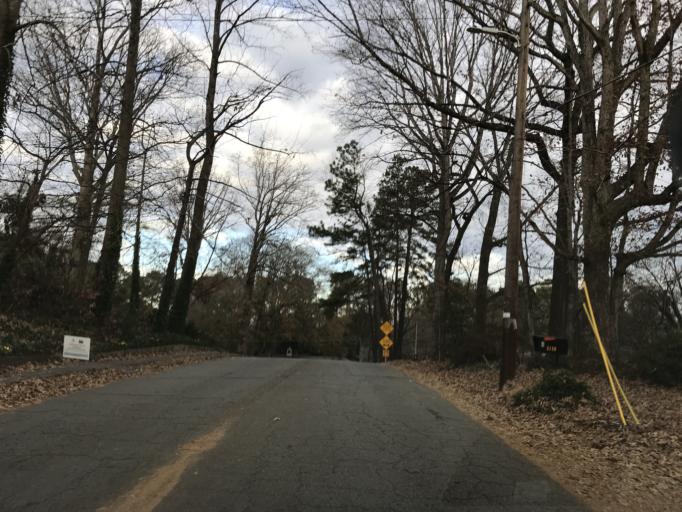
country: US
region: Georgia
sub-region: DeKalb County
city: Doraville
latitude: 33.8780
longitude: -84.2512
